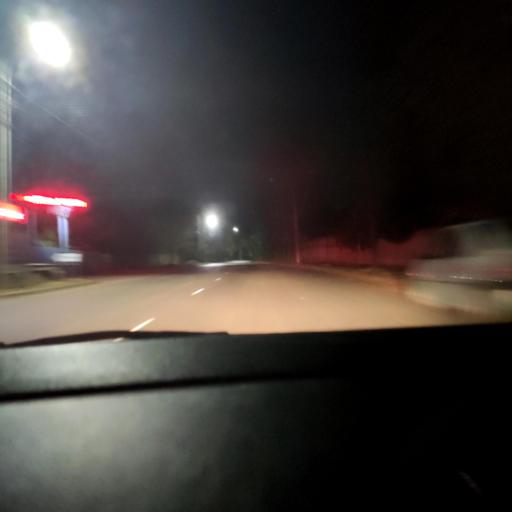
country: RU
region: Voronezj
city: Voronezh
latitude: 51.6868
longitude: 39.1751
